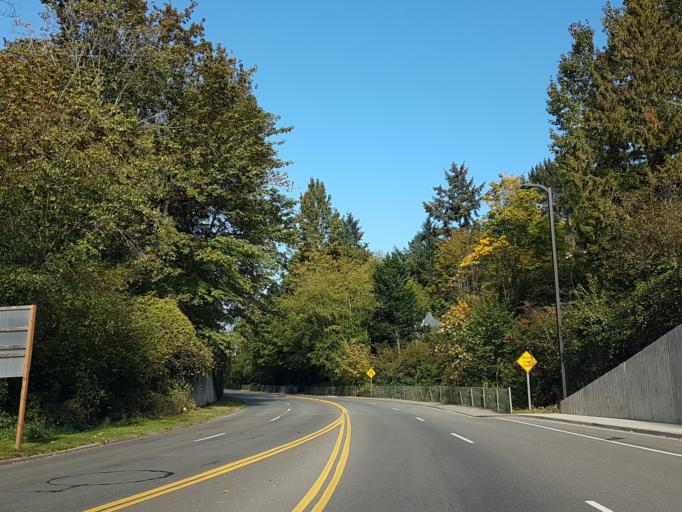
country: US
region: Washington
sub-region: King County
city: Kenmore
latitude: 47.7597
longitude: -122.2617
